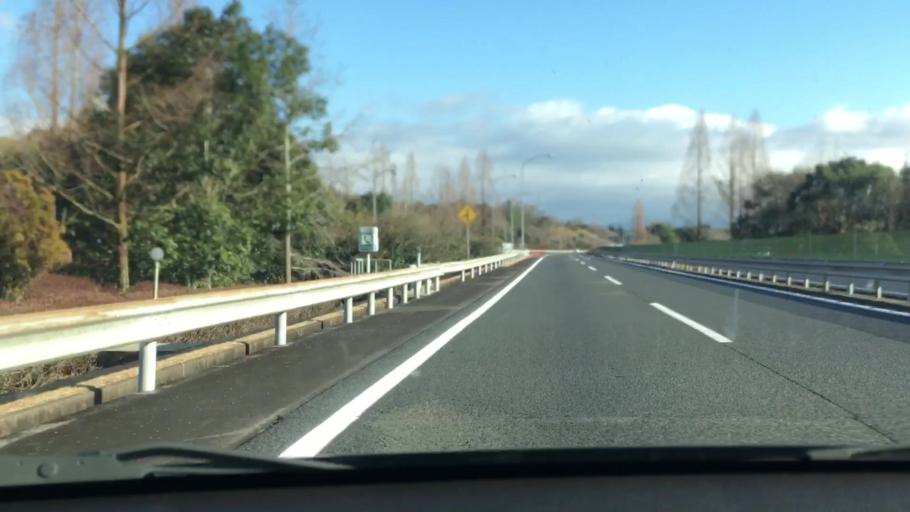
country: JP
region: Kumamoto
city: Hitoyoshi
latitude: 32.2328
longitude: 130.7692
